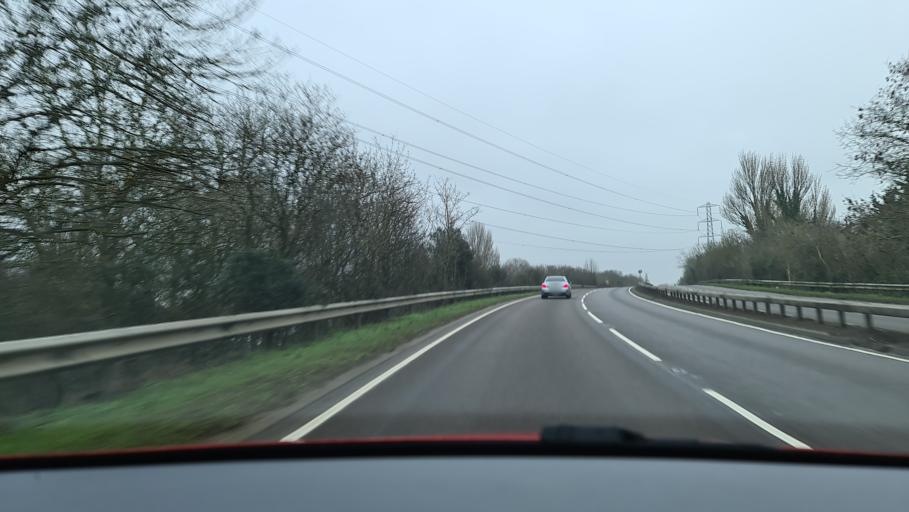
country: GB
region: England
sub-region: Surrey
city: Staines
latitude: 51.4305
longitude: -0.4822
